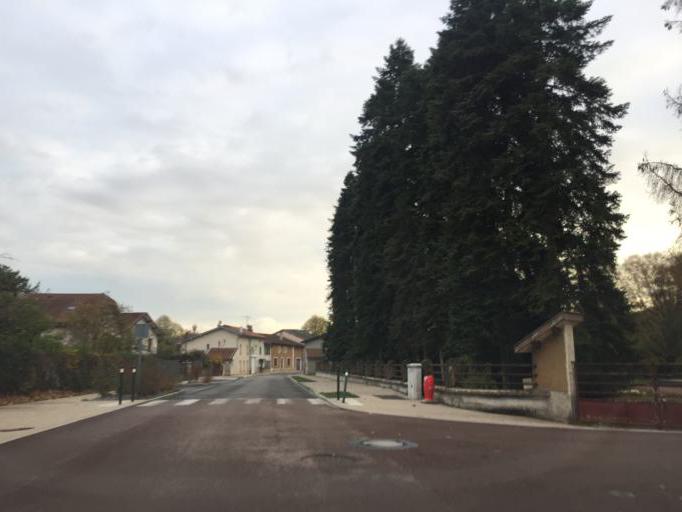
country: FR
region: Rhone-Alpes
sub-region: Departement de l'Ain
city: Chatillon-la-Palud
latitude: 45.9479
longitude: 5.2459
